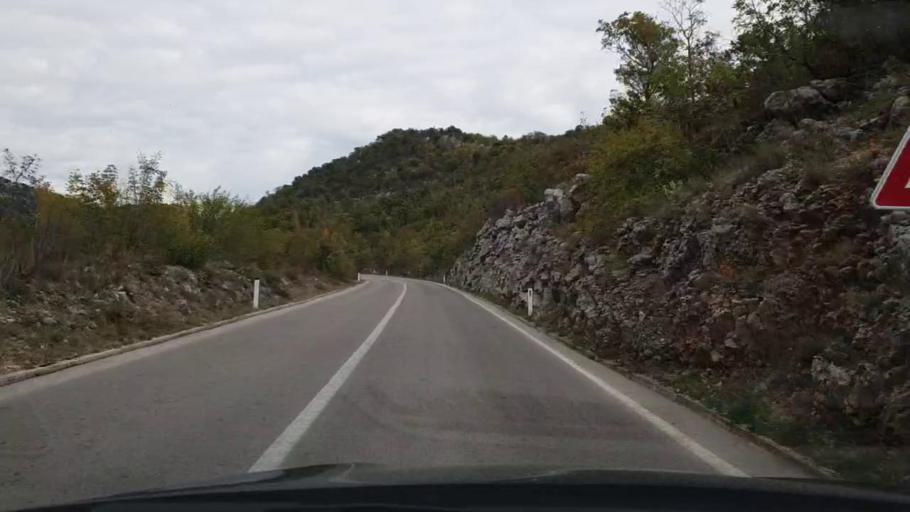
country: HR
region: Dubrovacko-Neretvanska
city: Cibaca
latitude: 42.6677
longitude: 18.2203
